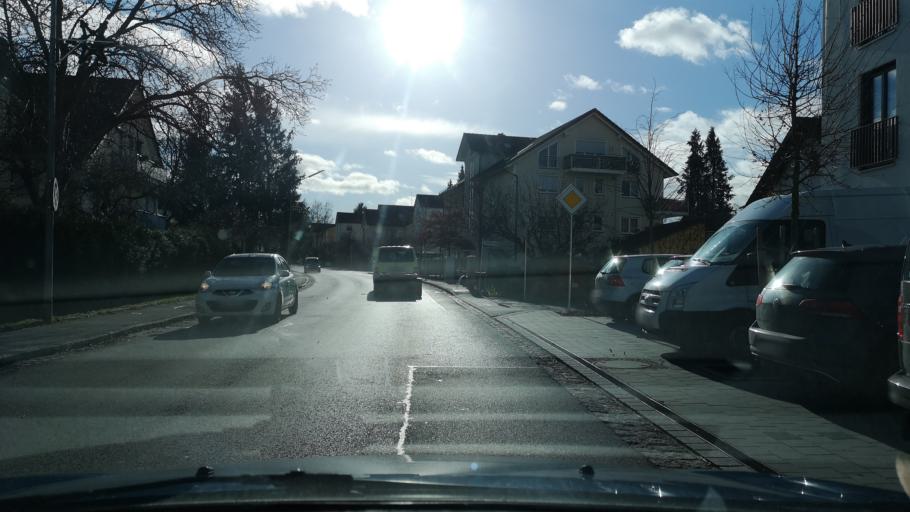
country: DE
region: Bavaria
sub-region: Upper Bavaria
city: Poing
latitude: 48.1696
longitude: 11.8118
